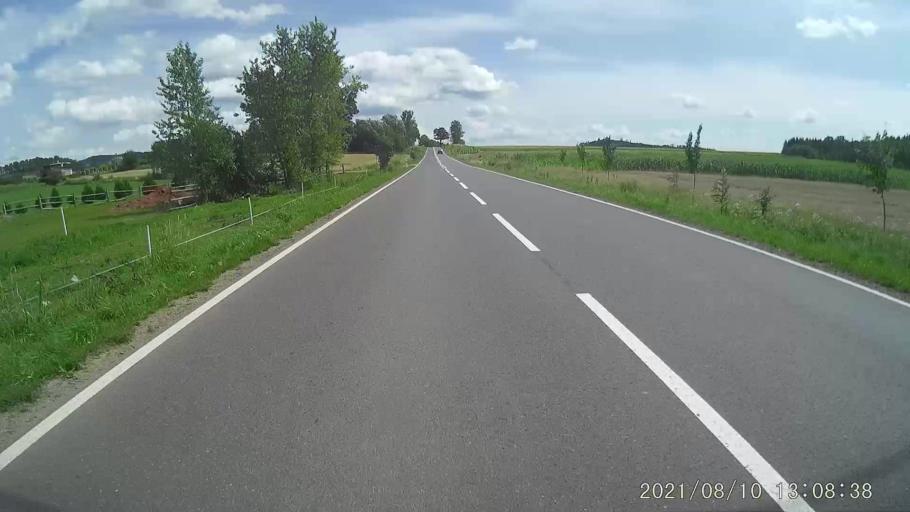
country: PL
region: Lower Silesian Voivodeship
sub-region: Powiat klodzki
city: Bozkow
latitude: 50.4941
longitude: 16.5537
